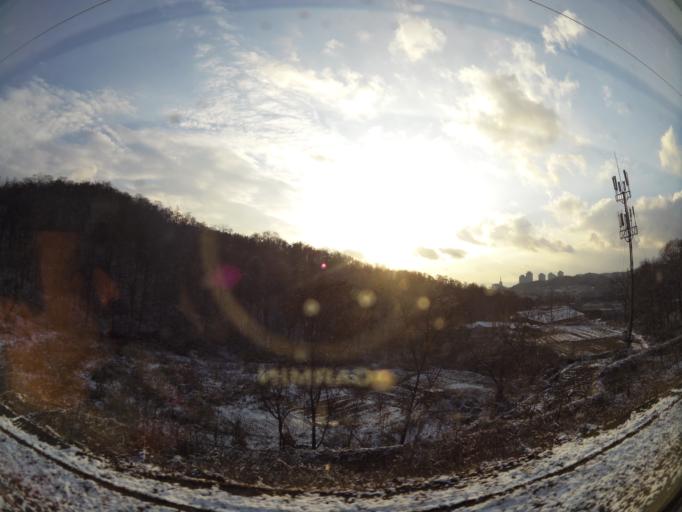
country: KR
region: Daejeon
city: Songgang-dong
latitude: 36.3823
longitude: 127.4167
